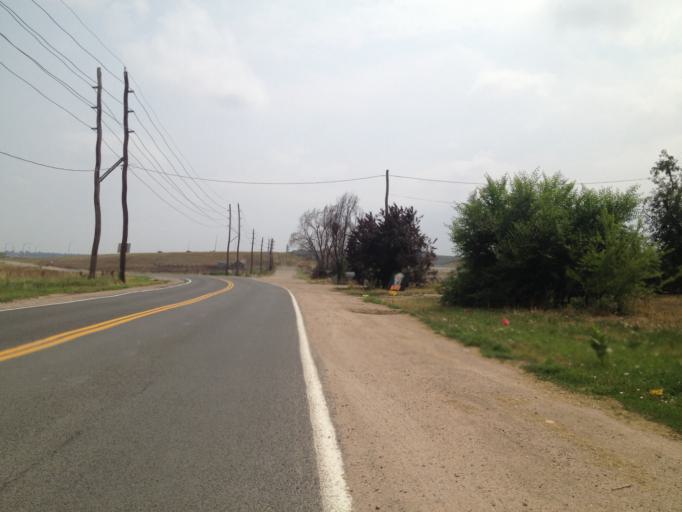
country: US
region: Colorado
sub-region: Broomfield County
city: Broomfield
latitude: 39.9054
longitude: -105.0811
